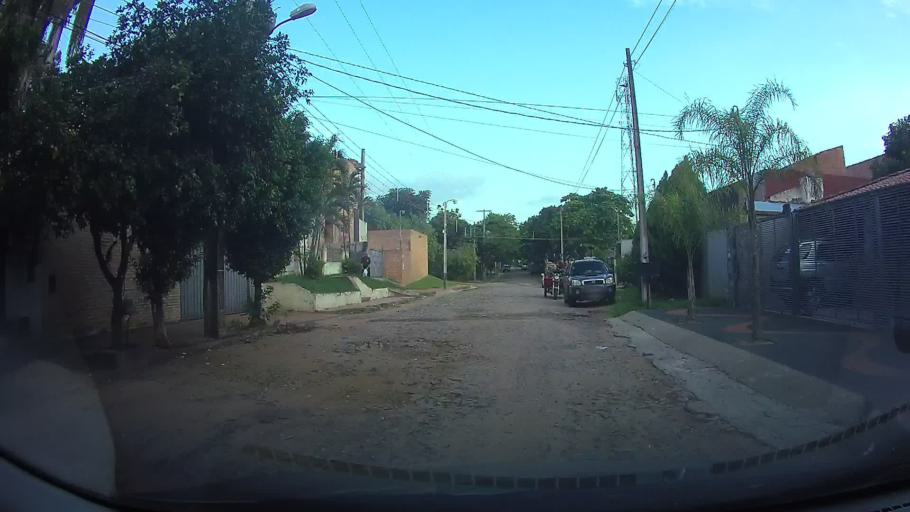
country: PY
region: Asuncion
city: Asuncion
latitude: -25.2685
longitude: -57.5727
